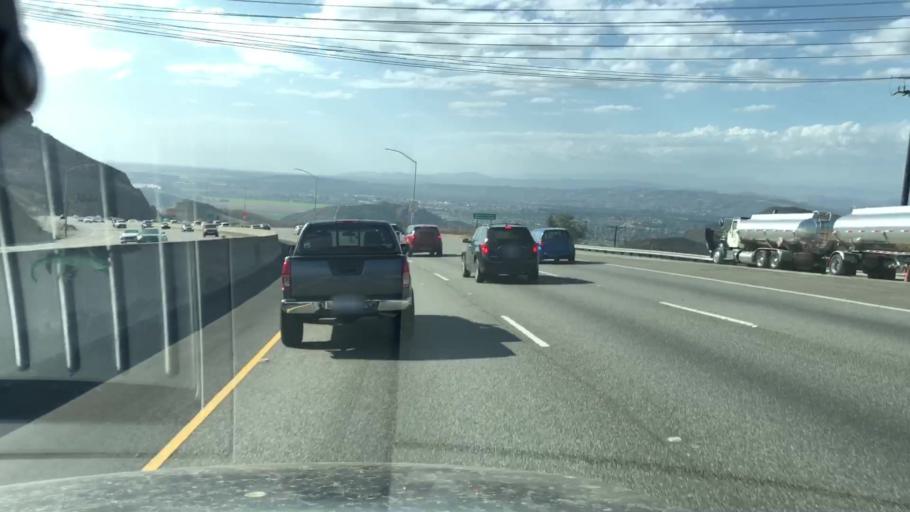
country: US
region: California
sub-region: Ventura County
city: Casa Conejo
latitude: 34.1990
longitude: -118.9570
